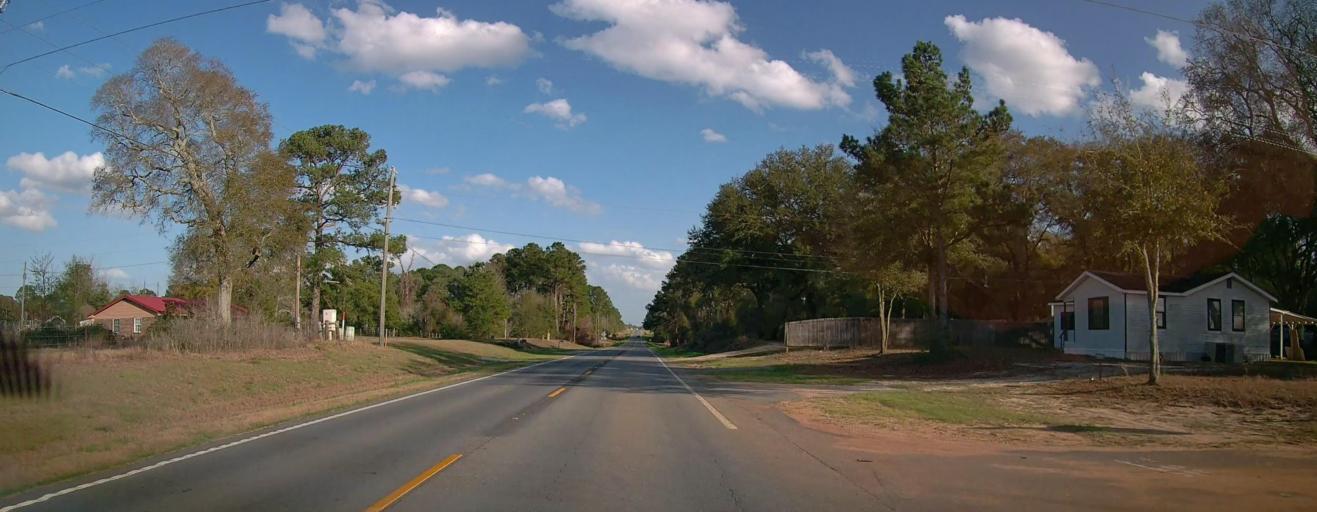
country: US
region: Georgia
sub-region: Tattnall County
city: Reidsville
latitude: 32.1094
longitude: -82.1763
